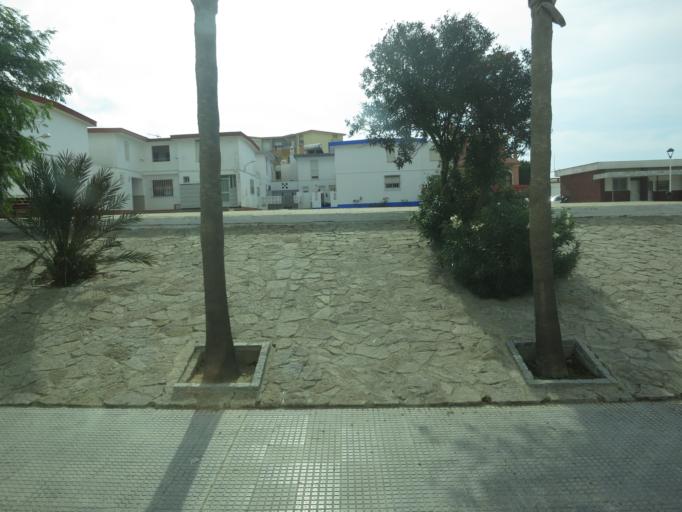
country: ES
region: Andalusia
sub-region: Provincia de Cadiz
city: Tarifa
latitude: 36.0182
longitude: -5.6006
